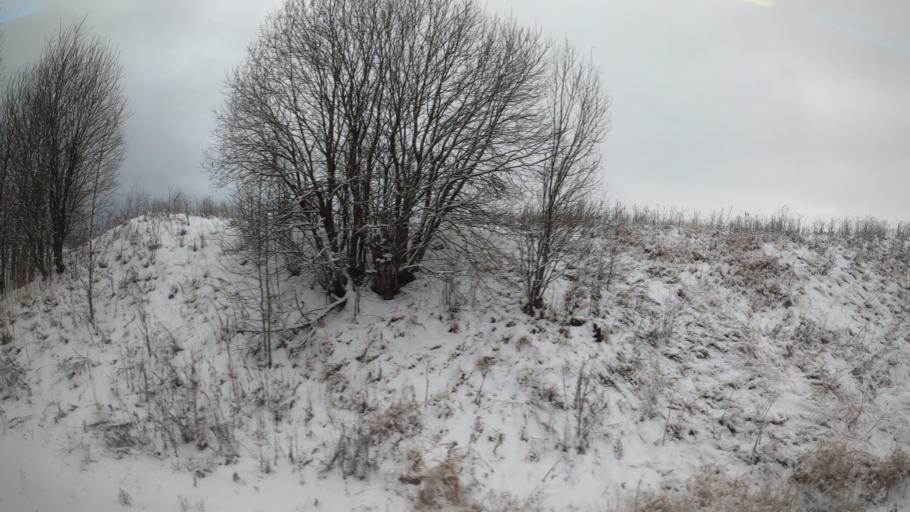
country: RU
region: Jaroslavl
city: Pereslavl'-Zalesskiy
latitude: 56.7031
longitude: 38.9107
